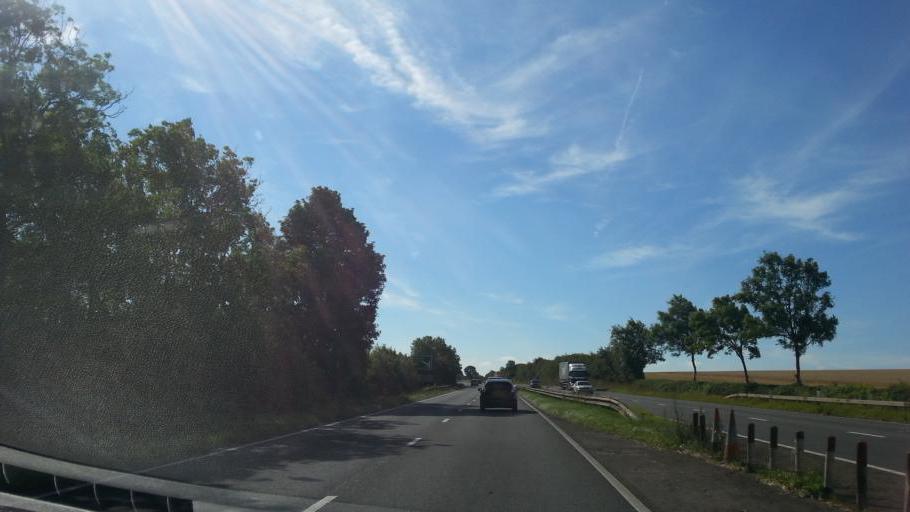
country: GB
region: England
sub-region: District of Rutland
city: Tickencote
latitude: 52.6655
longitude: -0.5239
